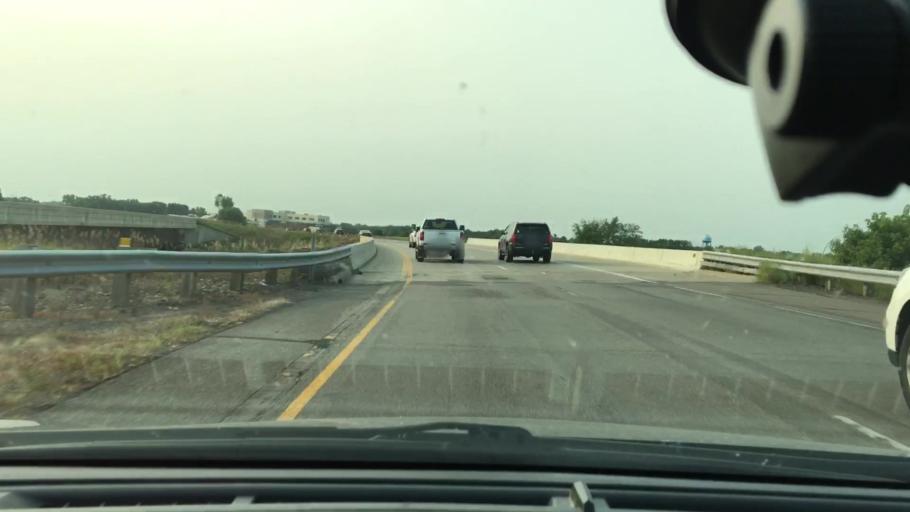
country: US
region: Minnesota
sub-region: Mille Lacs County
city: Princeton
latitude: 45.5537
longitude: -93.5846
